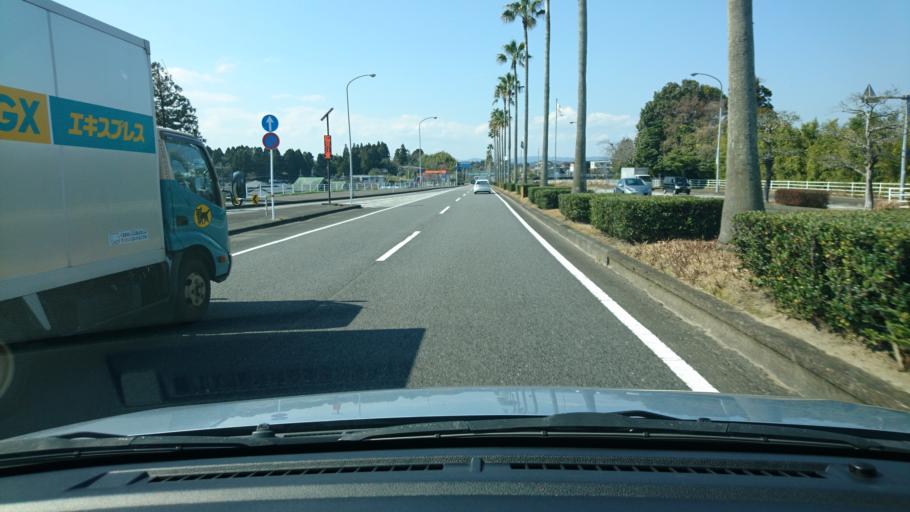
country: JP
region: Miyazaki
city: Miyazaki-shi
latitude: 31.8675
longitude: 131.4296
